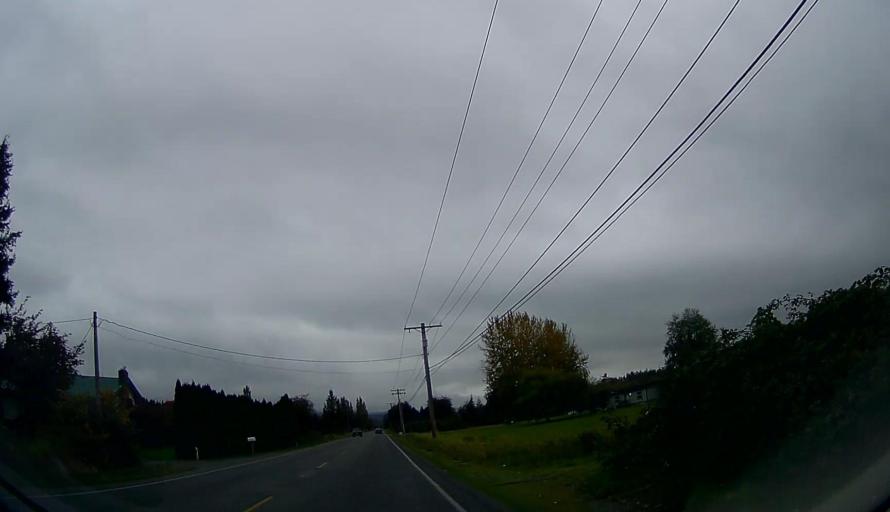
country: US
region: Washington
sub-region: Skagit County
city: Sedro-Woolley
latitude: 48.5100
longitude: -122.1992
